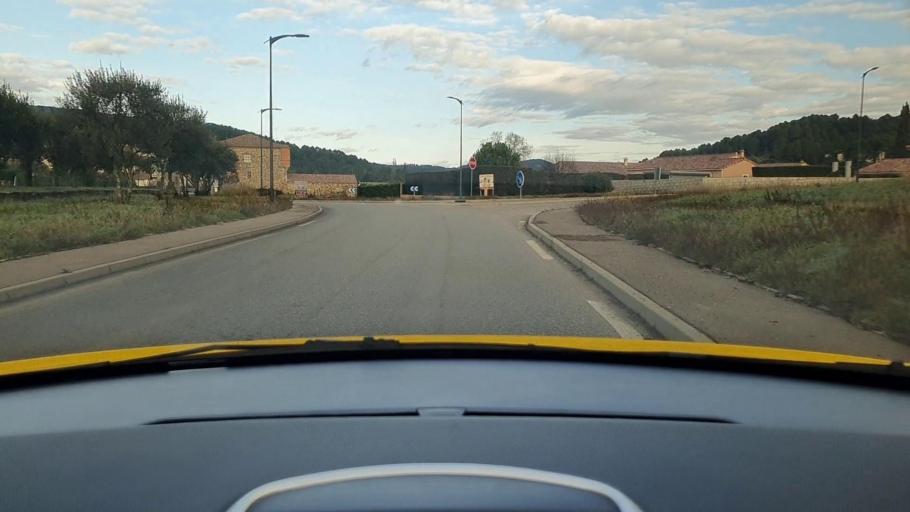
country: FR
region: Languedoc-Roussillon
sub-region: Departement du Gard
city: Laval-Pradel
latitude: 44.2288
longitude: 4.0620
